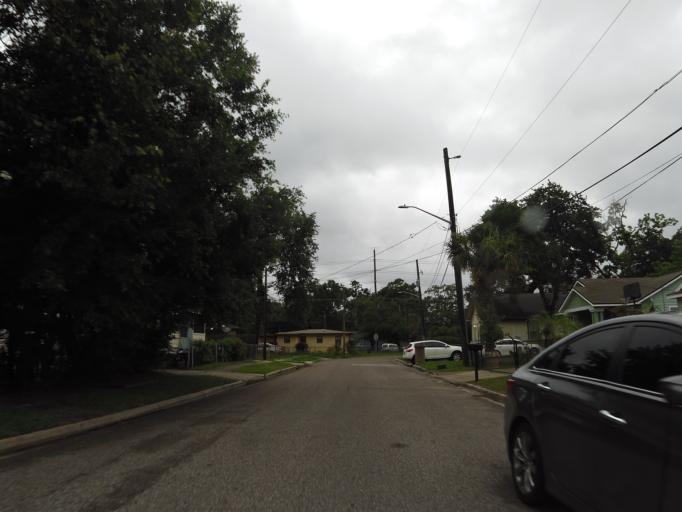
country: US
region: Florida
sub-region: Duval County
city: Jacksonville
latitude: 30.3498
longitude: -81.6331
